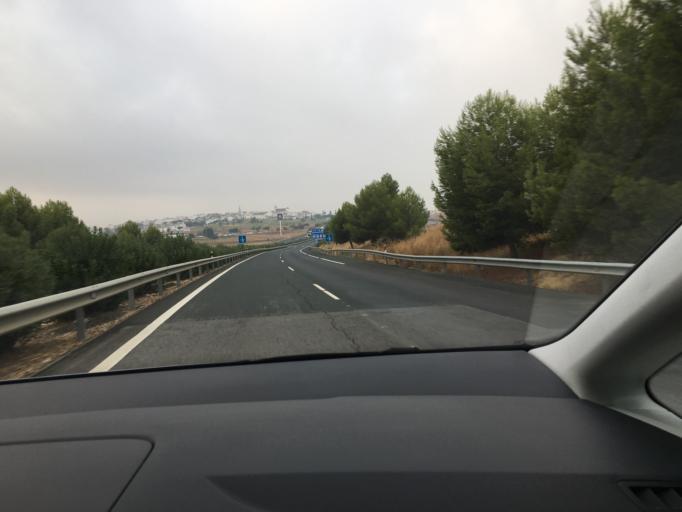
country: ES
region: Andalusia
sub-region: Province of Cordoba
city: La Carlota
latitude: 37.6844
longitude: -4.9250
